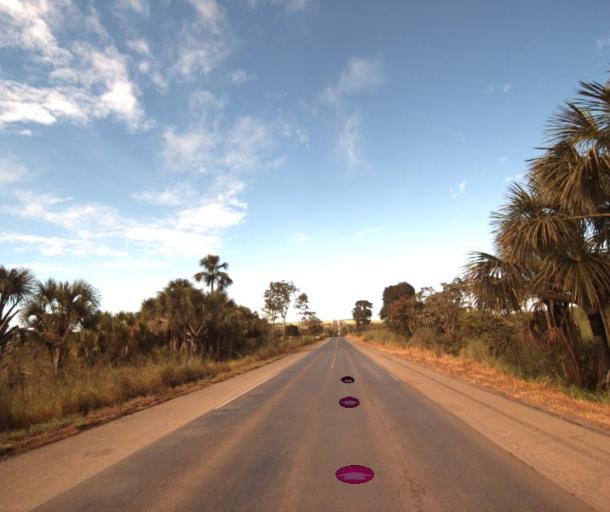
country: BR
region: Goias
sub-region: Itapaci
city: Itapaci
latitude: -14.8061
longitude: -49.2885
